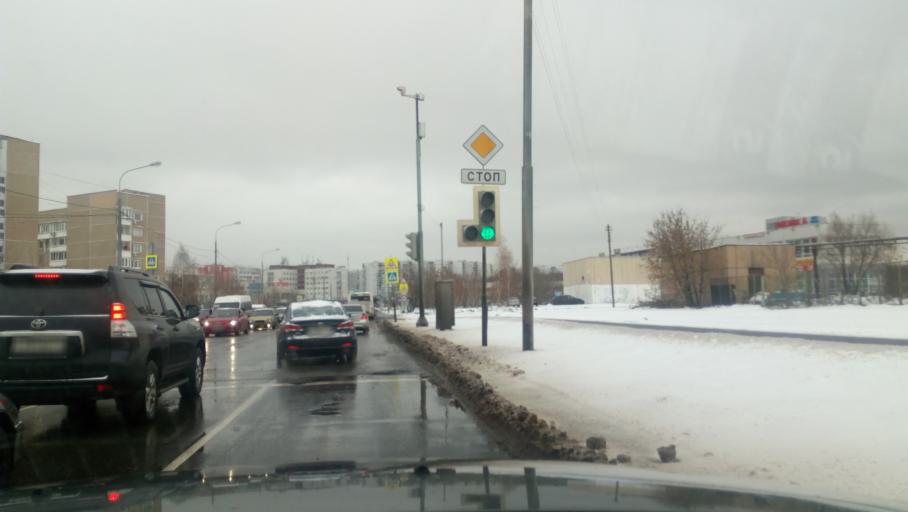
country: RU
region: Moskovskaya
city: Reutov
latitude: 55.7304
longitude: 37.8611
